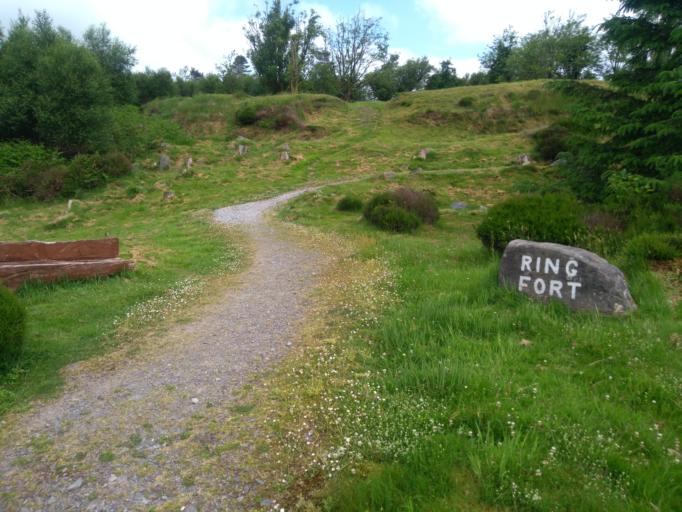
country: IE
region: Munster
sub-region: Ciarrai
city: Kenmare
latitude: 51.8312
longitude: -9.5132
